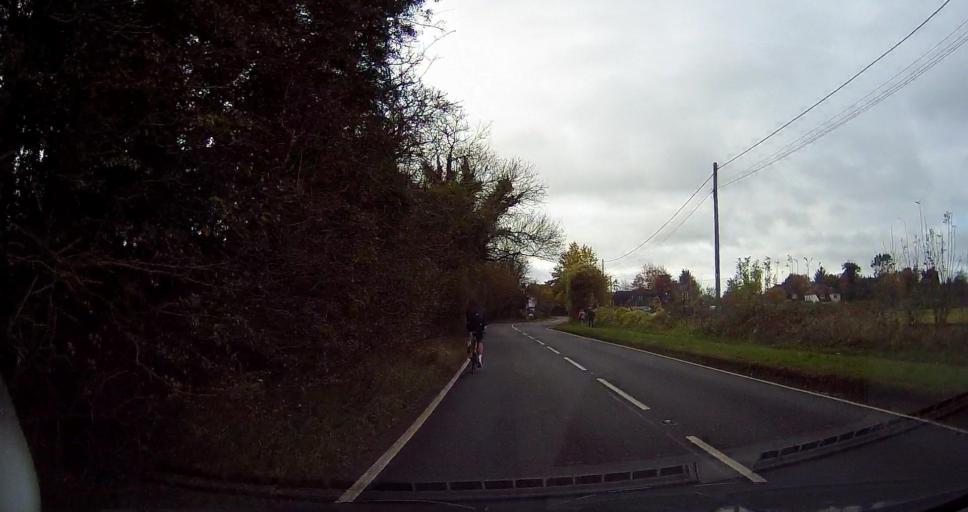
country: GB
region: England
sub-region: Kent
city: Meopham
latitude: 51.3493
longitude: 0.3495
